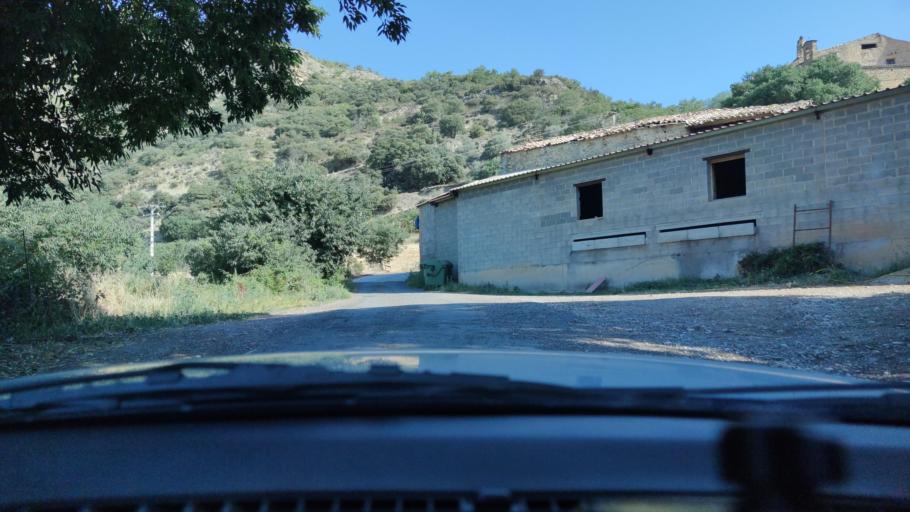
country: ES
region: Catalonia
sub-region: Provincia de Lleida
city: Llimiana
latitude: 42.0853
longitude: 0.8410
